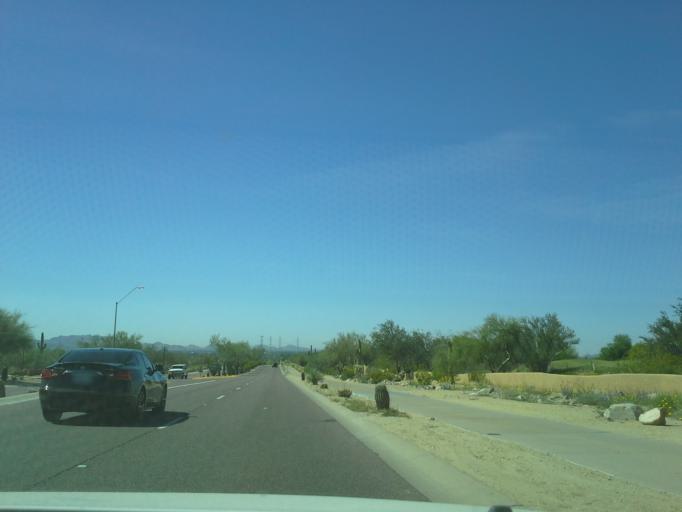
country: US
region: Arizona
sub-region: Maricopa County
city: Scottsdale
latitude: 33.5898
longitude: -111.8278
